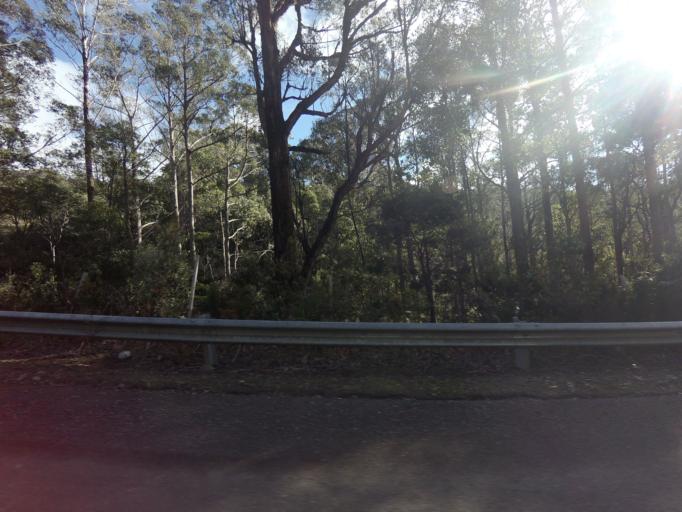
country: AU
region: Tasmania
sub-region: Glenorchy
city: Berriedale
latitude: -42.8387
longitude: 147.1655
